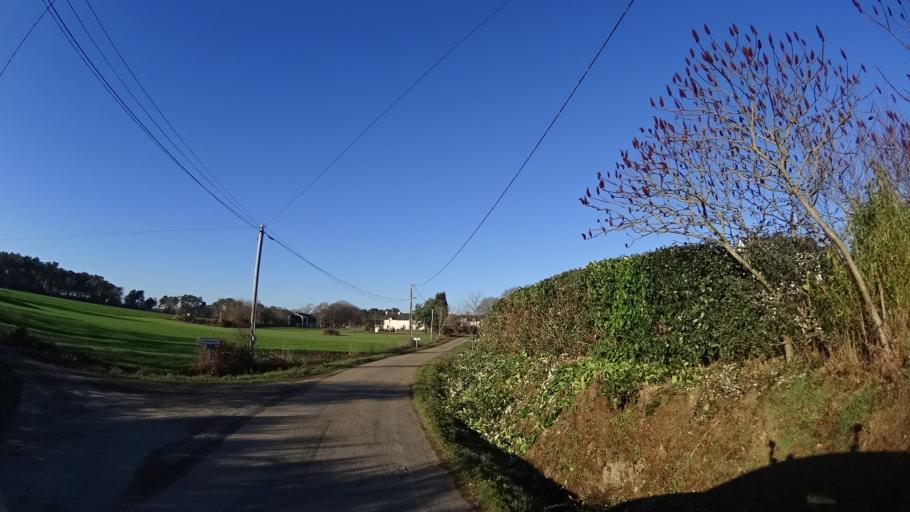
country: FR
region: Brittany
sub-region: Departement du Morbihan
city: Allaire
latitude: 47.6604
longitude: -2.1832
